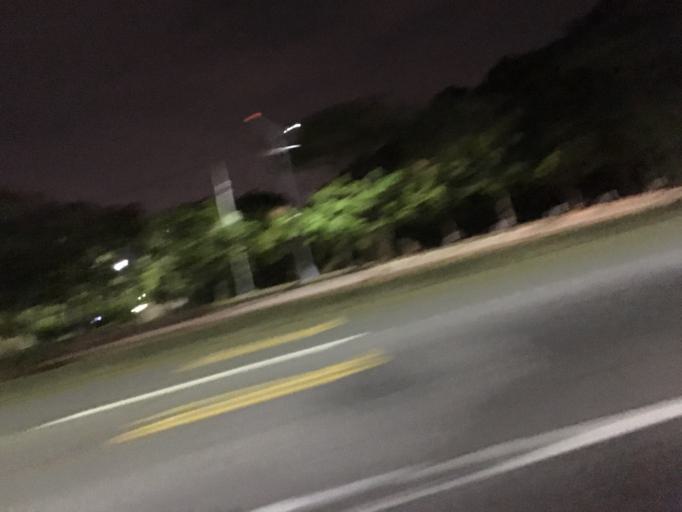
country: TW
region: Taiwan
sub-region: Hsinchu
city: Hsinchu
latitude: 24.7831
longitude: 120.9541
